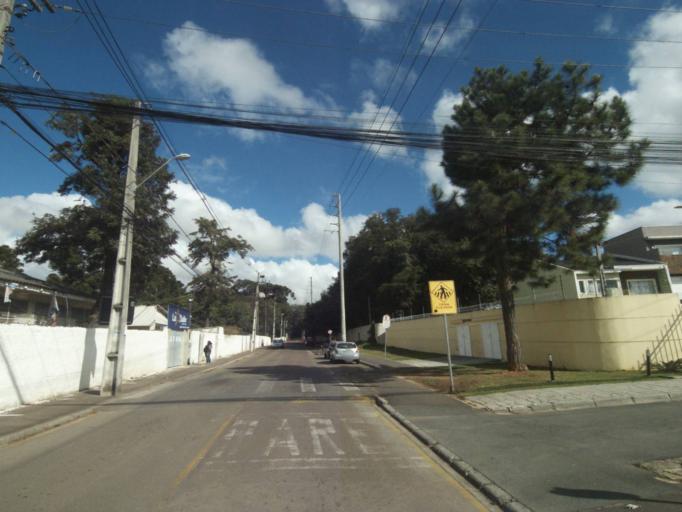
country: BR
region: Parana
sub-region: Sao Jose Dos Pinhais
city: Sao Jose dos Pinhais
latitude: -25.5320
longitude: -49.2918
